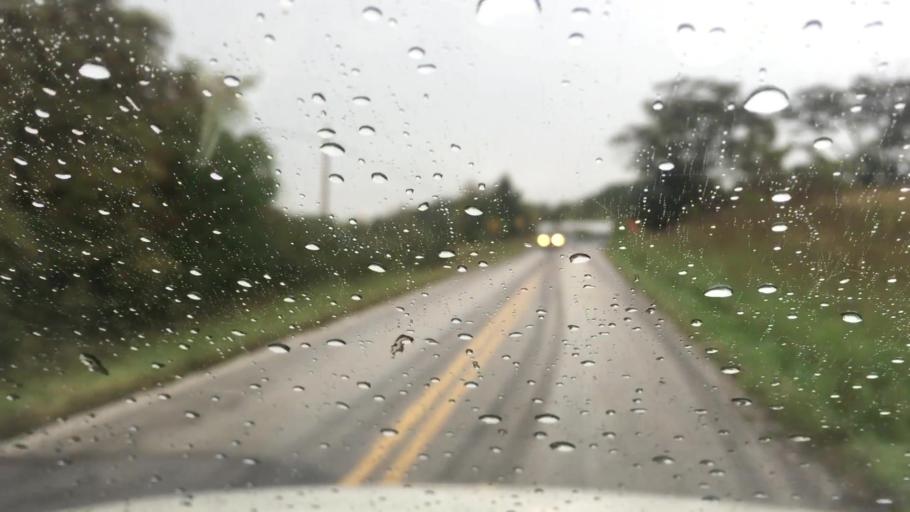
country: US
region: Missouri
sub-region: Boone County
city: Columbia
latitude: 38.9424
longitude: -92.4967
